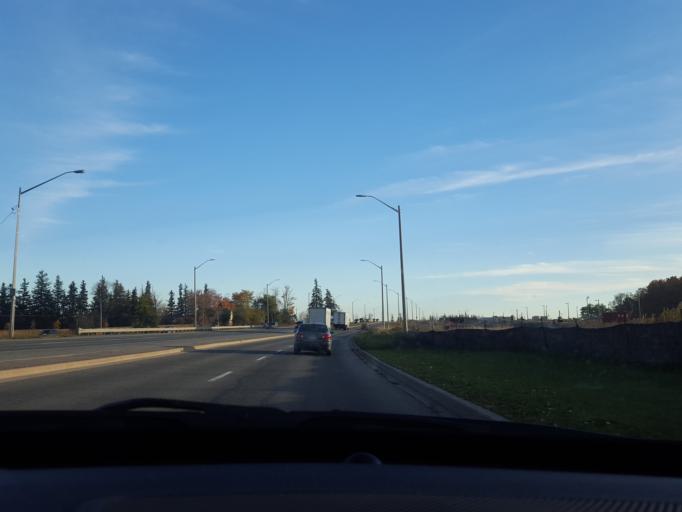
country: CA
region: Ontario
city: Markham
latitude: 43.8975
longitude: -79.2146
